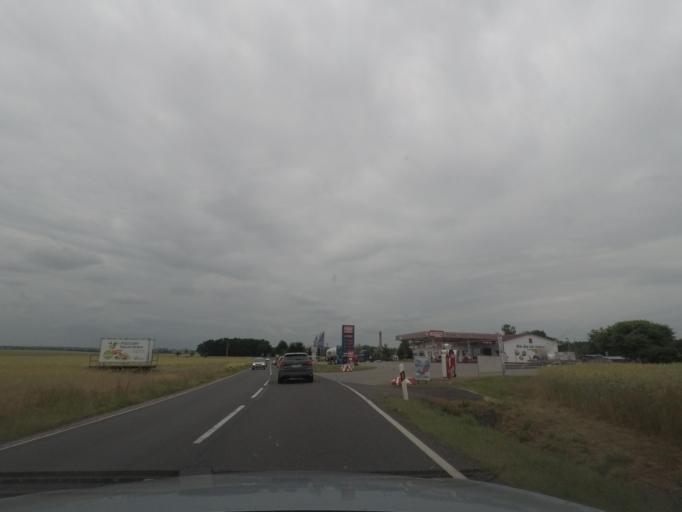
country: DE
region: Saxony-Anhalt
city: Haldensleben I
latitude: 52.2646
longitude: 11.3703
